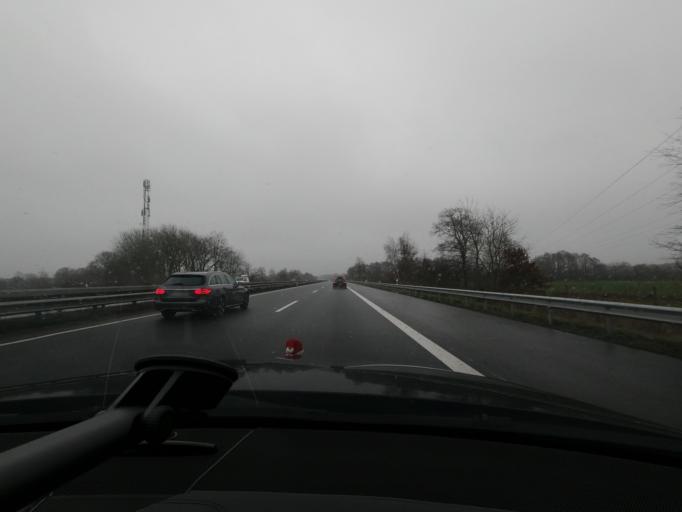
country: DE
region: Schleswig-Holstein
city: Bokel
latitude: 54.2456
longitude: 9.8152
